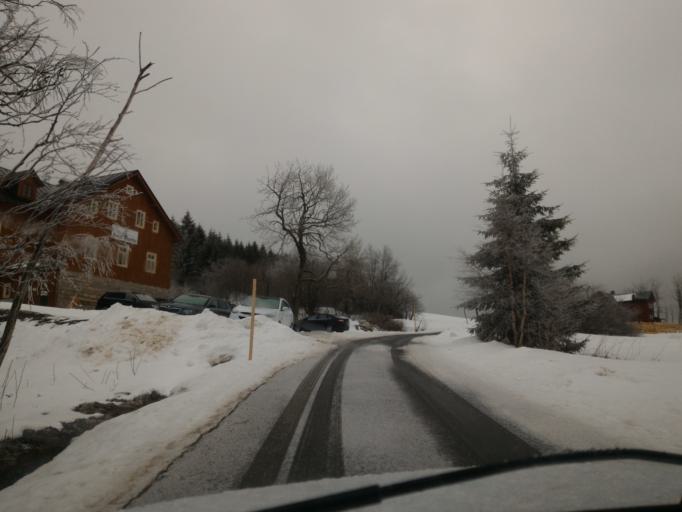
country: CZ
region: Liberecky
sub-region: Okres Jablonec nad Nisou
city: Korenov
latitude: 50.8151
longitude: 15.3516
